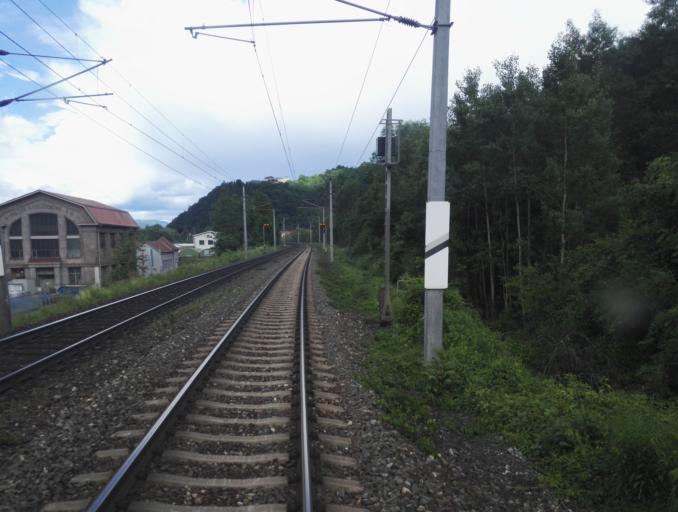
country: AT
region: Styria
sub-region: Politischer Bezirk Bruck-Muerzzuschlag
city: Bruck an der Mur
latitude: 47.4339
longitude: 15.2784
